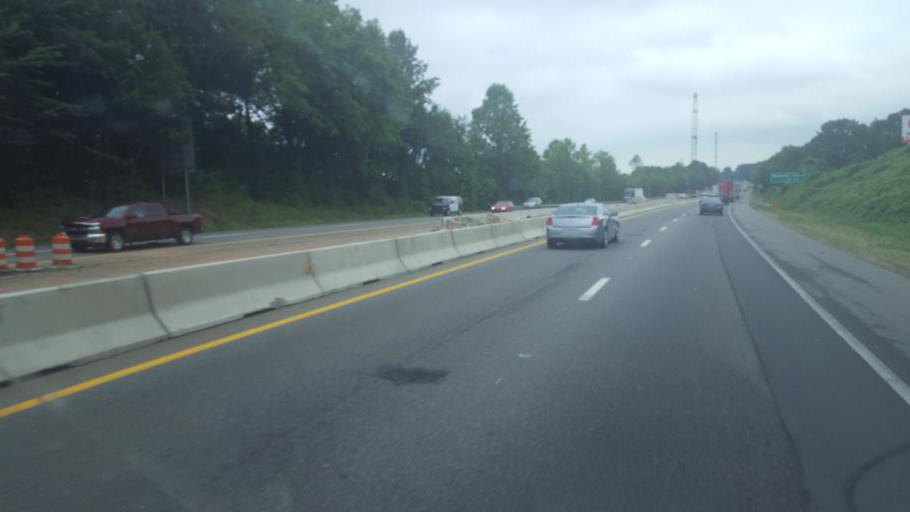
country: US
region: North Carolina
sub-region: Iredell County
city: Mooresville
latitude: 35.5641
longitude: -80.8584
